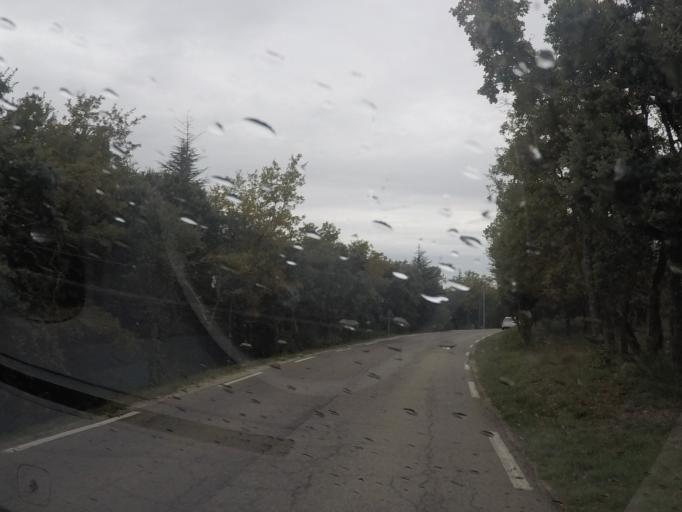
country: FR
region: Provence-Alpes-Cote d'Azur
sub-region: Departement du Vaucluse
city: Bonnieux
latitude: 43.8173
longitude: 5.3204
